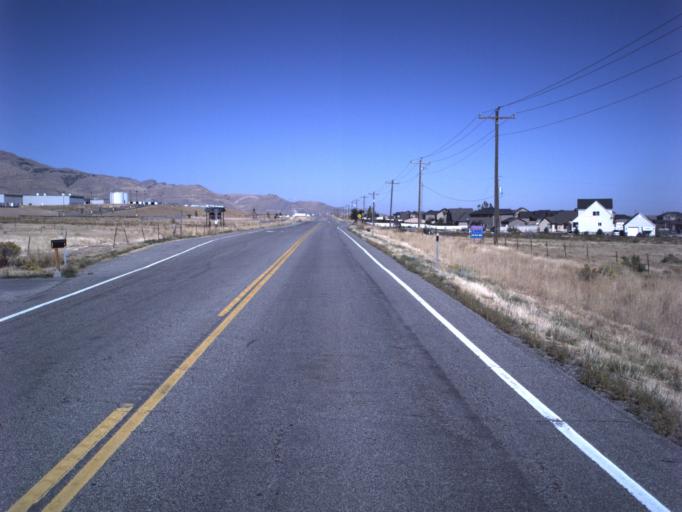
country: US
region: Utah
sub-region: Tooele County
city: Grantsville
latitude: 40.6157
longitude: -112.4982
